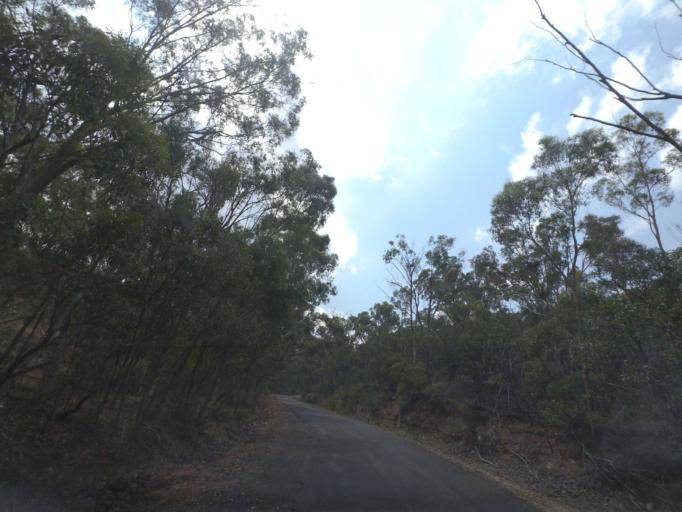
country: AU
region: Victoria
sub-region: Moorabool
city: Bacchus Marsh
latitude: -37.6000
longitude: 144.4327
